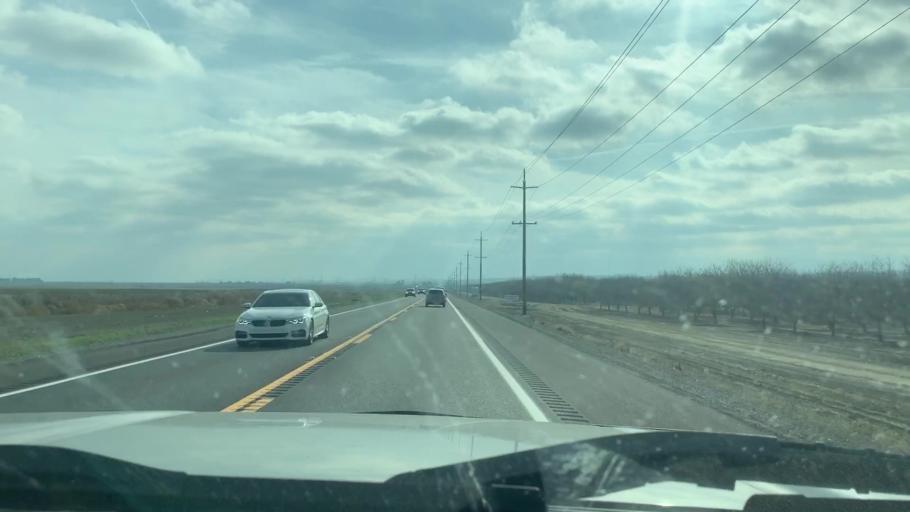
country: US
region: California
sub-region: Kings County
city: Kettleman City
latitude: 36.0320
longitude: -119.9591
